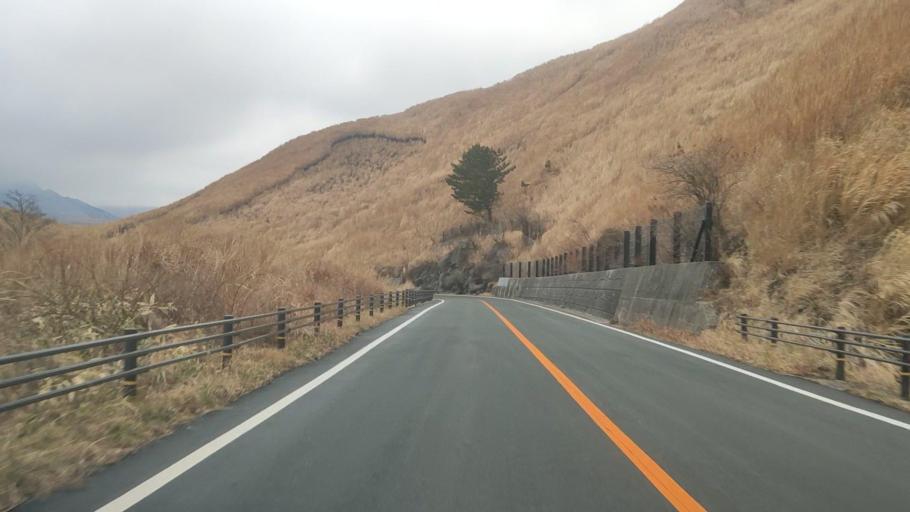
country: JP
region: Kumamoto
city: Aso
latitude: 32.9053
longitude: 131.1482
